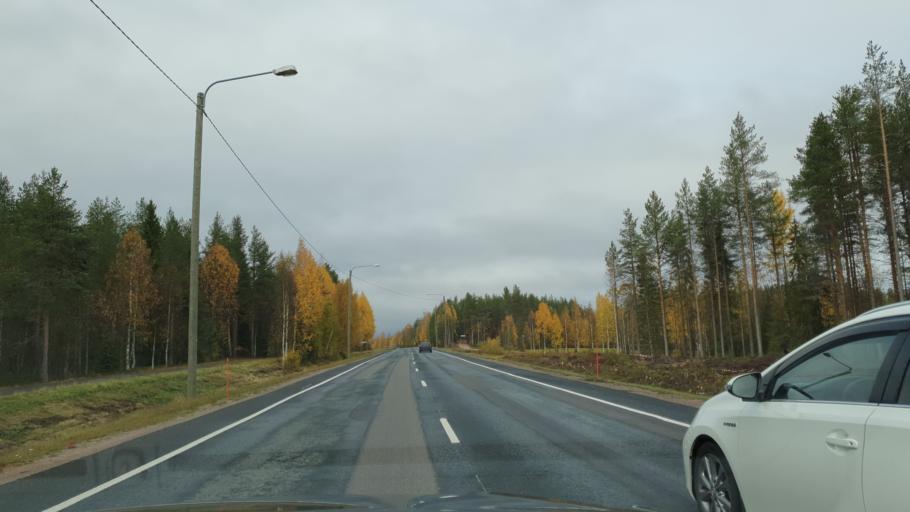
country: FI
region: Lapland
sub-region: Rovaniemi
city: Rovaniemi
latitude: 66.6385
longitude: 25.4916
